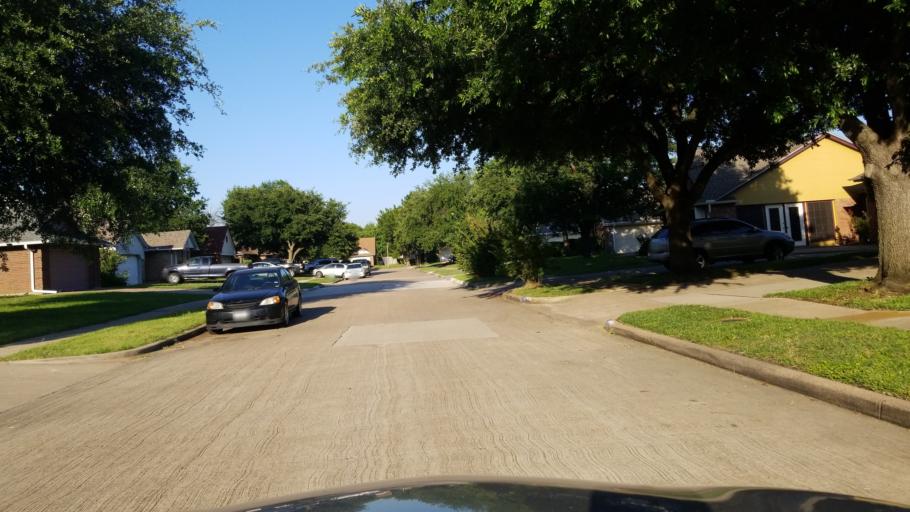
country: US
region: Texas
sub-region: Dallas County
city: Grand Prairie
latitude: 32.6835
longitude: -97.0413
